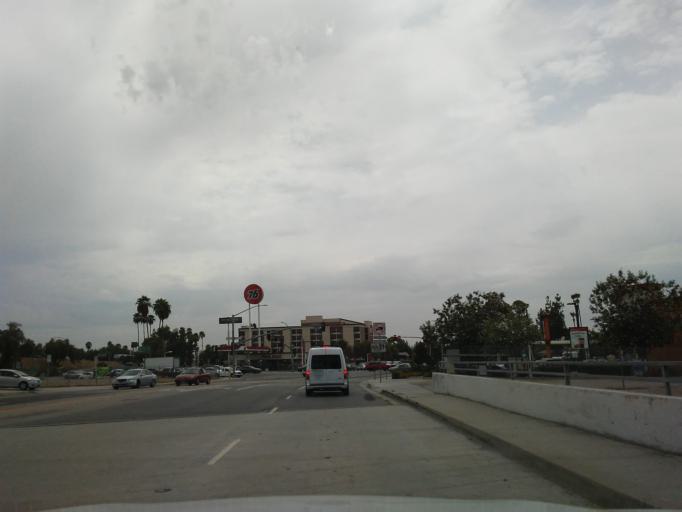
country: US
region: California
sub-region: San Bernardino County
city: Loma Linda
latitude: 34.0661
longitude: -117.2775
